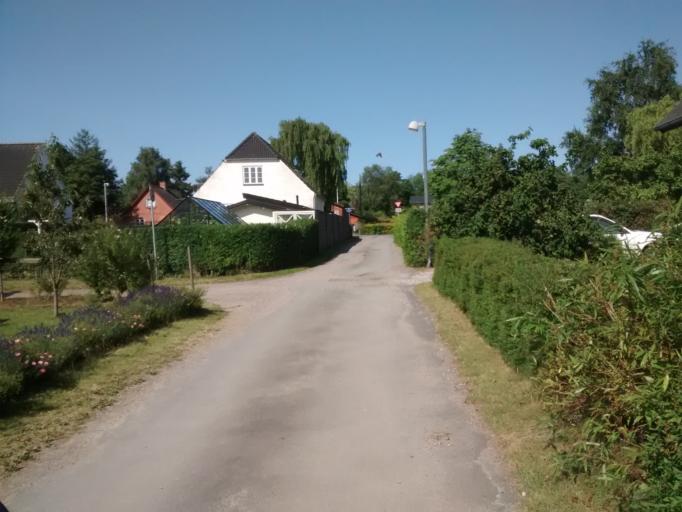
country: DK
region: Zealand
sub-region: Soro Kommune
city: Soro
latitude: 55.4615
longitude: 11.5538
